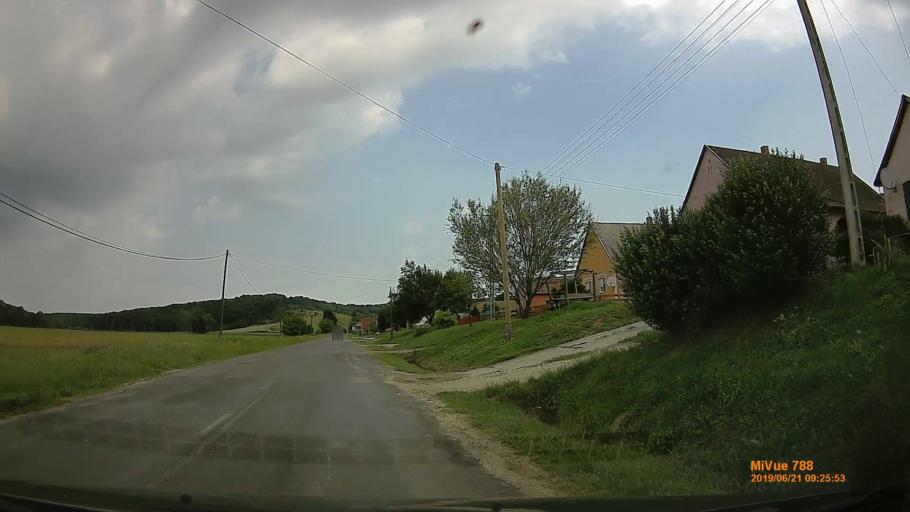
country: HU
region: Somogy
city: Taszar
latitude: 46.2688
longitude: 17.9061
